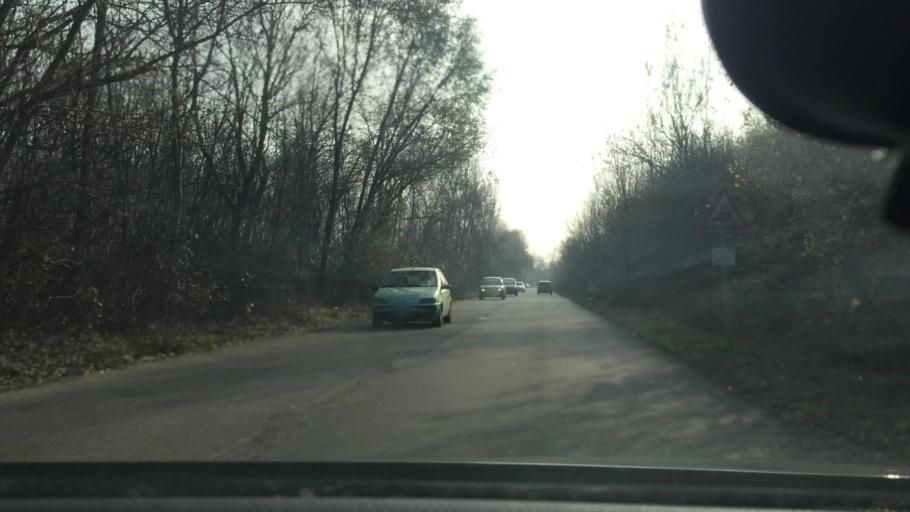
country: IT
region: Lombardy
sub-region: Provincia di Monza e Brianza
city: Villaggio del Sole
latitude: 45.6018
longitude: 9.0965
